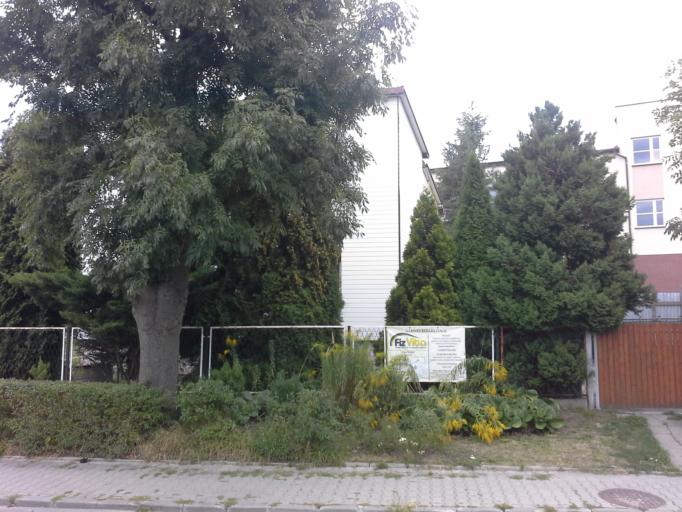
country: PL
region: Lesser Poland Voivodeship
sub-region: Powiat chrzanowski
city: Trzebinia
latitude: 50.1603
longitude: 19.4662
